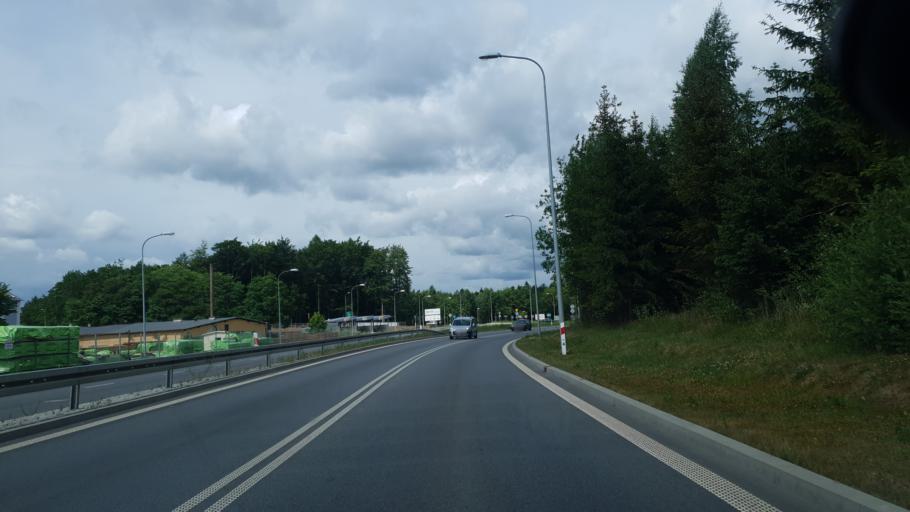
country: PL
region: Pomeranian Voivodeship
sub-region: Powiat kartuski
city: Kartuzy
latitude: 54.3377
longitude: 18.2095
